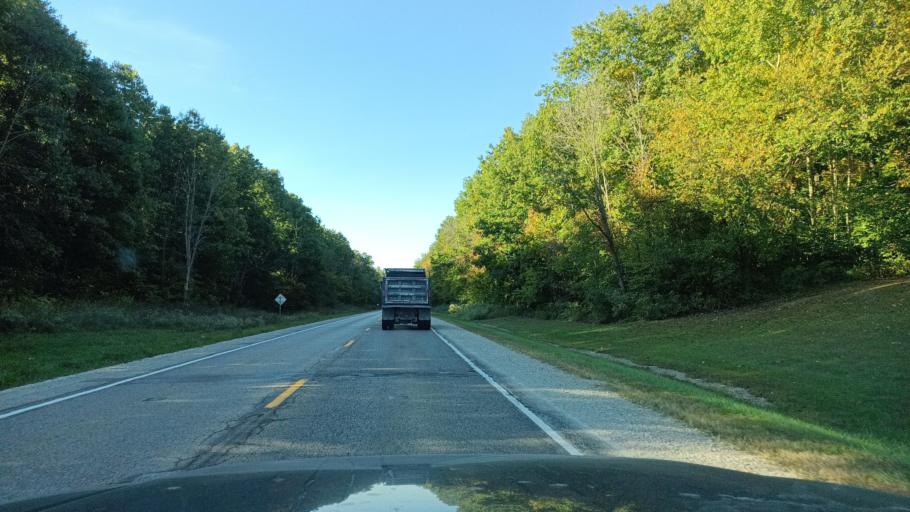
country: US
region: Illinois
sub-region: Clark County
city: Marshall
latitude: 39.4387
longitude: -87.6859
